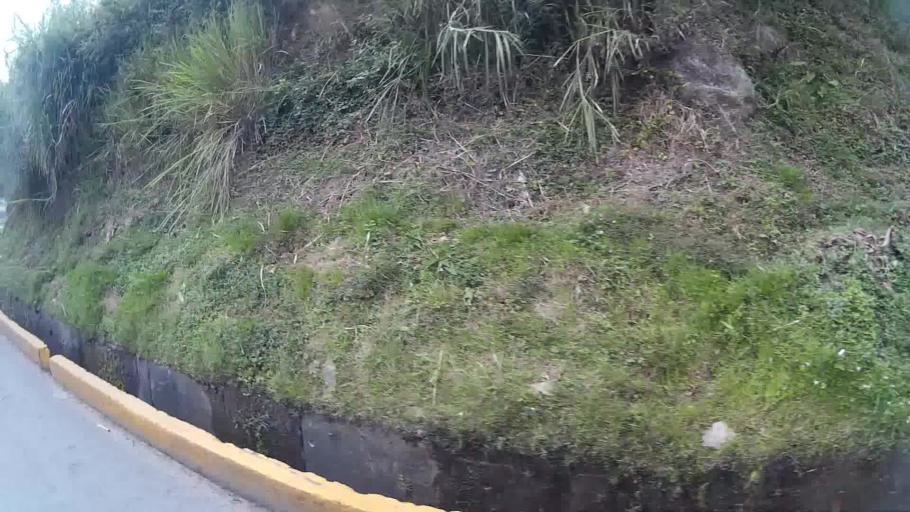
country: CO
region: Risaralda
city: Pereira
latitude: 4.8177
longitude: -75.7420
